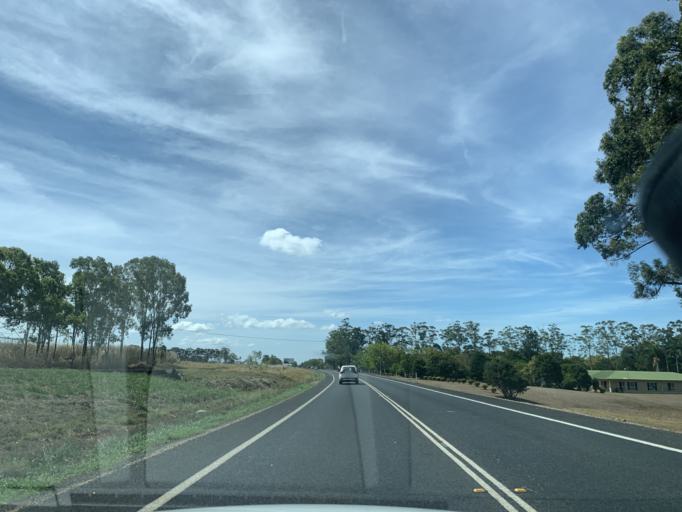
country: AU
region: Queensland
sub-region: Tablelands
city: Tolga
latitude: -17.2080
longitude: 145.4780
